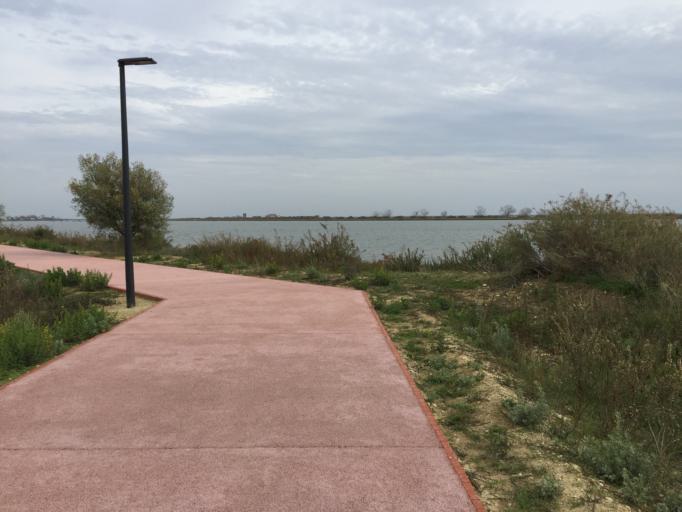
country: PT
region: Lisbon
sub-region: Vila Franca de Xira
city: Povoa de Santa Iria
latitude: 38.8508
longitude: -9.0673
